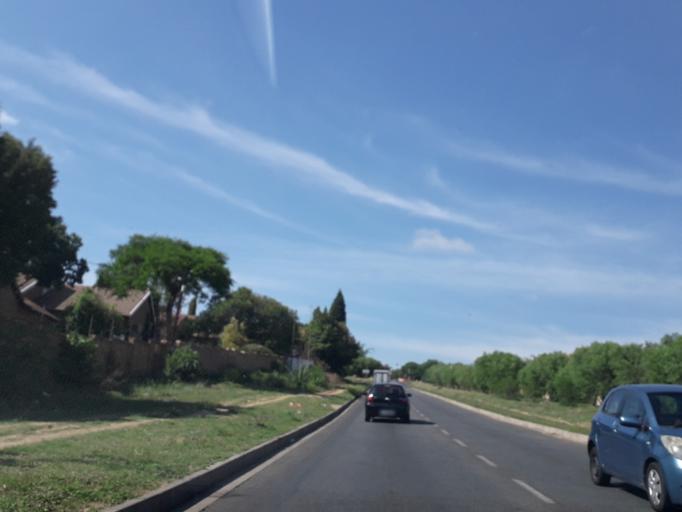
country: ZA
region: Gauteng
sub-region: City of Johannesburg Metropolitan Municipality
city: Roodepoort
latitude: -26.0803
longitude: 27.9583
